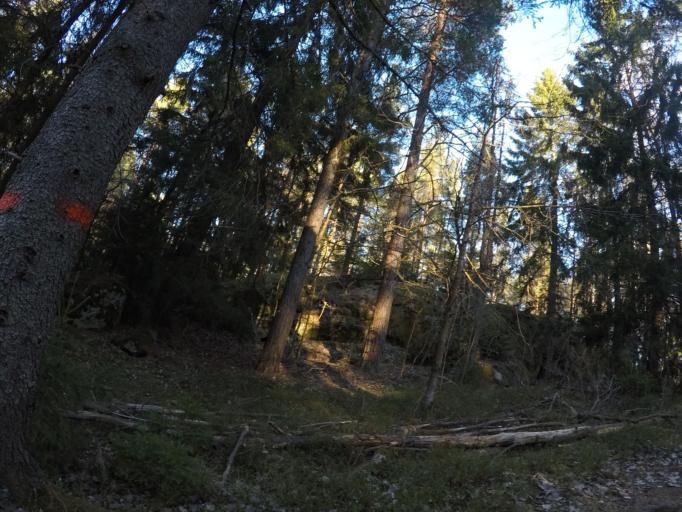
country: SE
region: Soedermanland
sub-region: Eskilstuna Kommun
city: Torshalla
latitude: 59.4104
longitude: 16.4940
